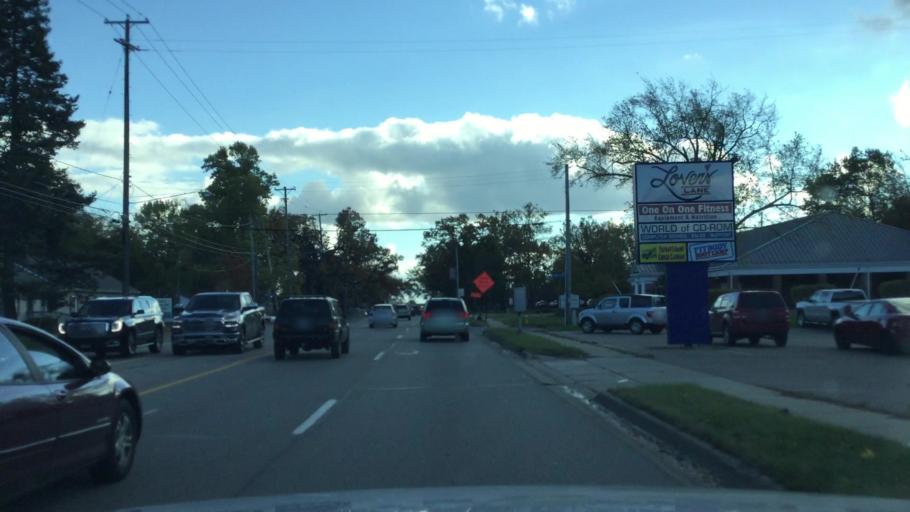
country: US
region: Michigan
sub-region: Kalamazoo County
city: Kalamazoo
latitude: 42.2511
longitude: -85.5897
